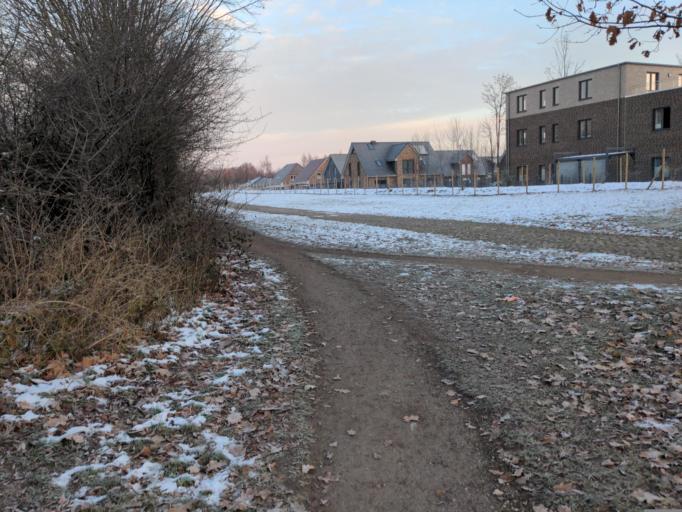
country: DE
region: Schleswig-Holstein
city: Stockelsdorf
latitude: 53.8695
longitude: 10.6347
